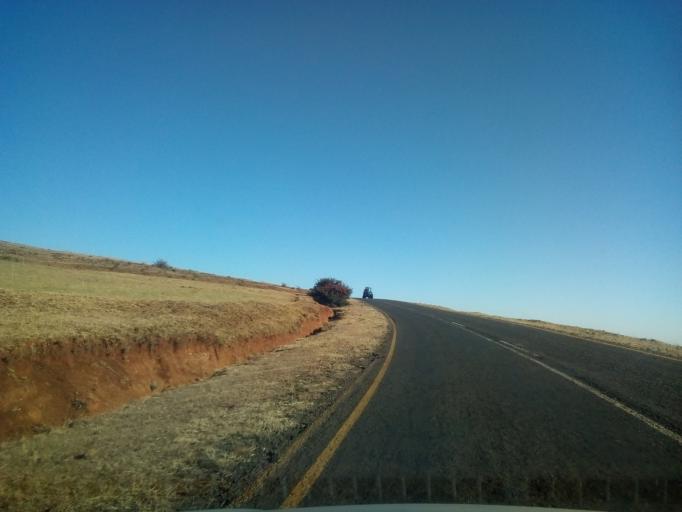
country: LS
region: Berea
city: Teyateyaneng
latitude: -29.2536
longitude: 27.7728
